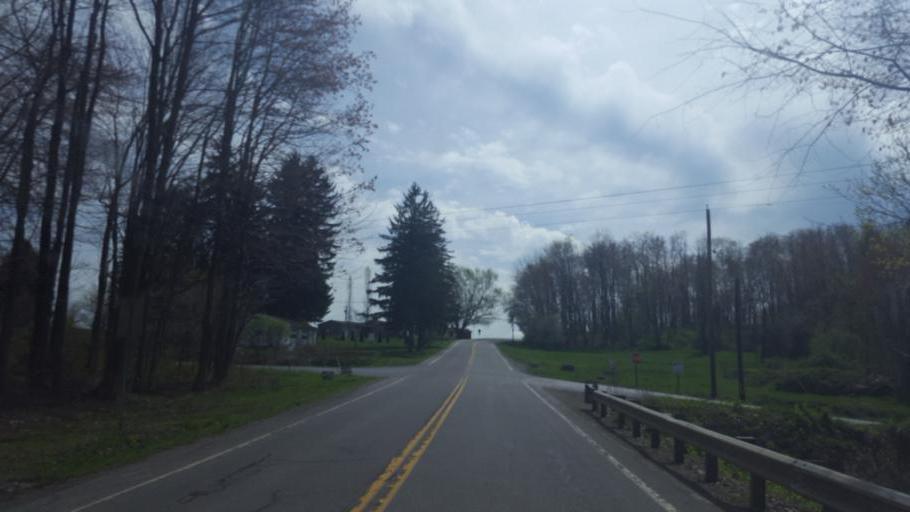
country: US
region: Pennsylvania
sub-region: Mercer County
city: Stoneboro
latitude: 41.3531
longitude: -79.9876
